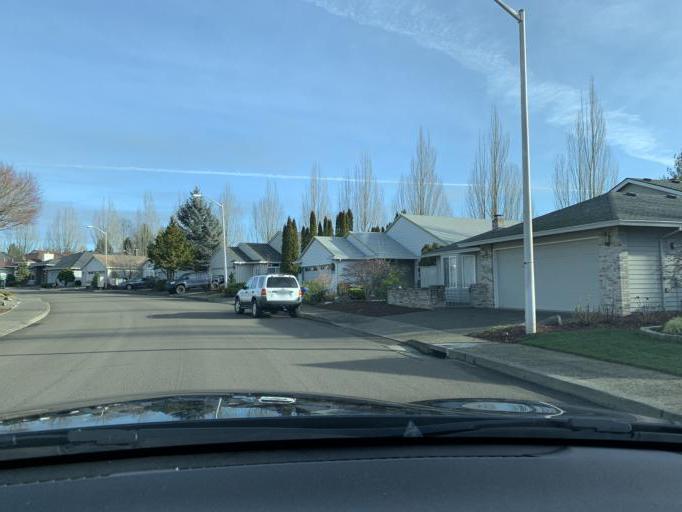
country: US
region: Washington
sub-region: Clark County
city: Mill Plain
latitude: 45.5948
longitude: -122.5085
